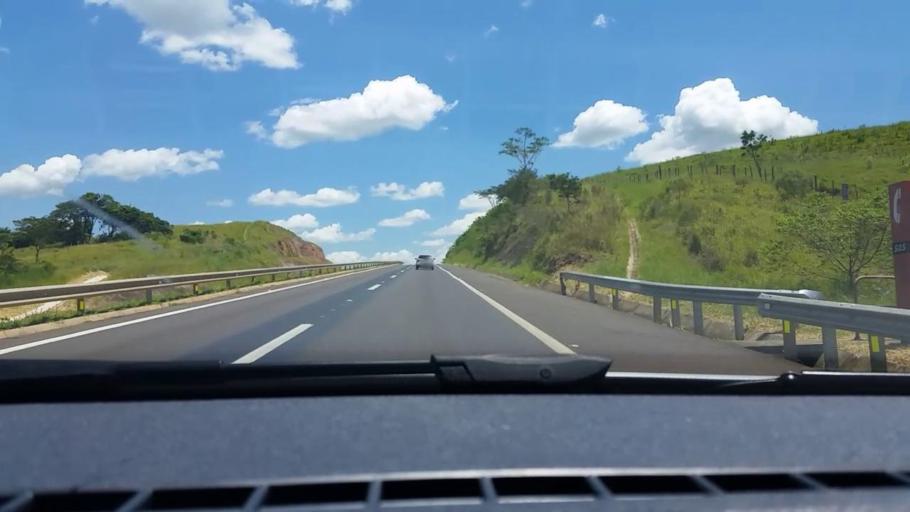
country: BR
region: Sao Paulo
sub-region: Bauru
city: Bauru
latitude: -22.4361
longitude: -49.1365
